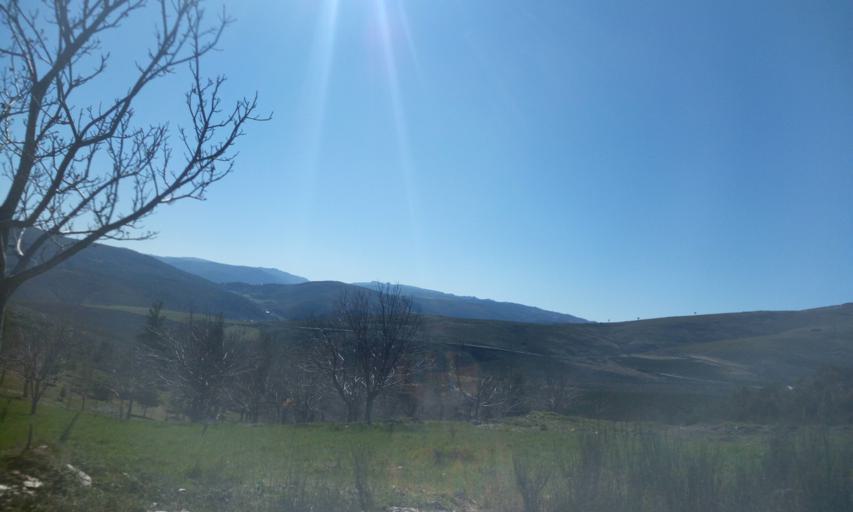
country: PT
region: Guarda
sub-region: Manteigas
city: Manteigas
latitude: 40.4701
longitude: -7.5036
